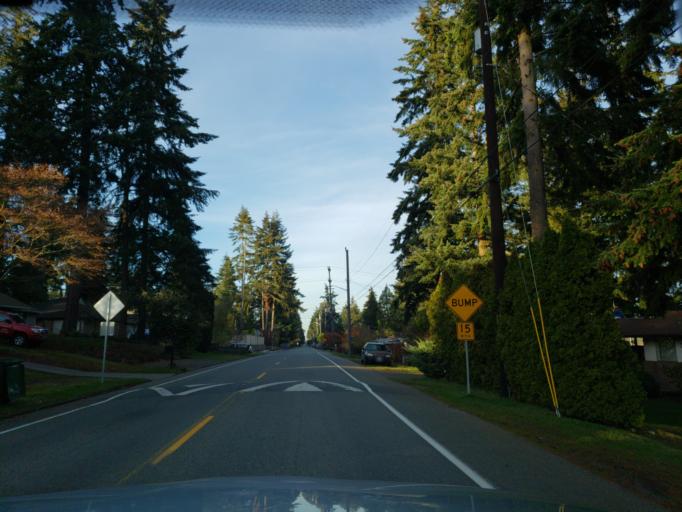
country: US
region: Washington
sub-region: King County
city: Shoreline
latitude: 47.7478
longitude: -122.3401
